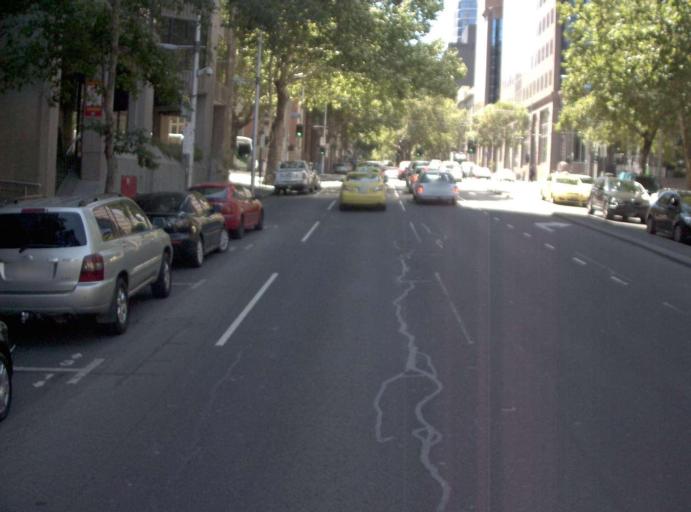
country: AU
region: Victoria
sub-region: Melbourne
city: Docklands
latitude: -37.8192
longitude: 144.9571
